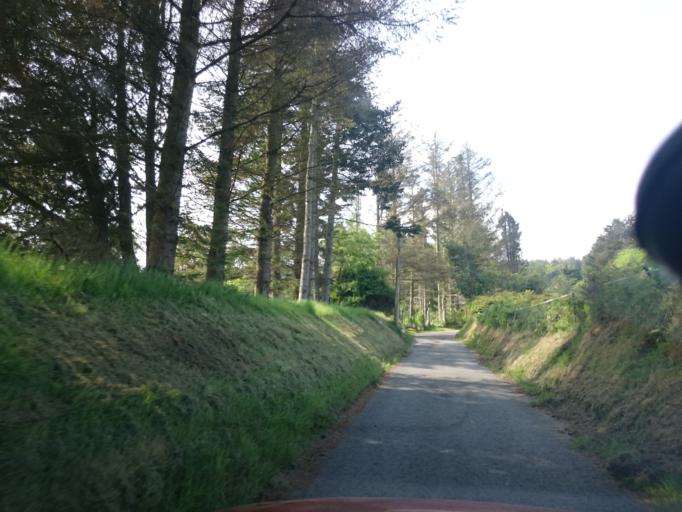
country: IE
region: Leinster
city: Ballinteer
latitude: 53.2491
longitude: -6.2517
